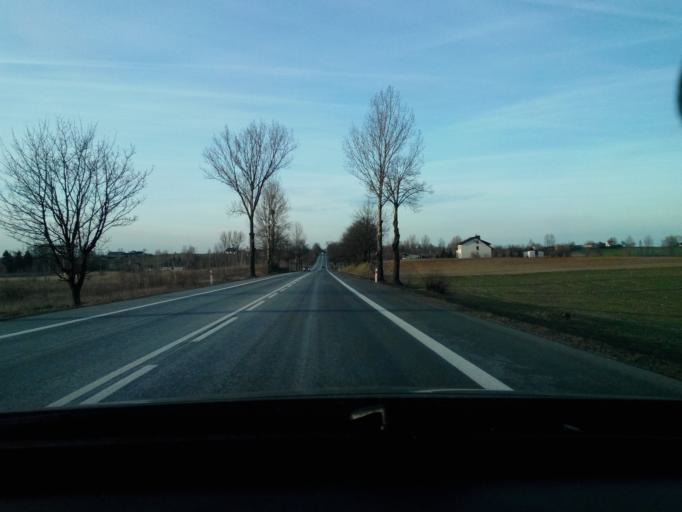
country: PL
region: Kujawsko-Pomorskie
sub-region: Powiat wloclawski
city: Lubien Kujawski
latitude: 52.4397
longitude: 19.1610
